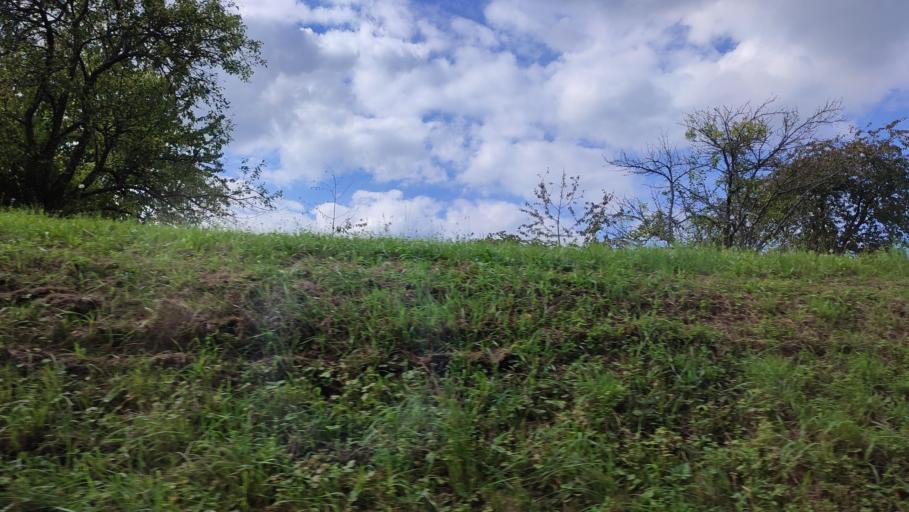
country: DE
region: Baden-Wuerttemberg
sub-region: Freiburg Region
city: Appenweier
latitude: 48.5247
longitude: 8.0066
